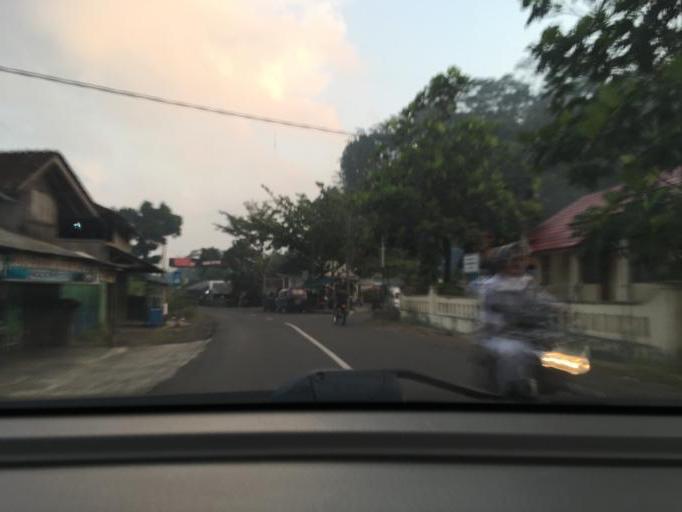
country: ID
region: West Java
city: Kampungdesa Pamokolan
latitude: -7.1958
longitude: 108.1994
